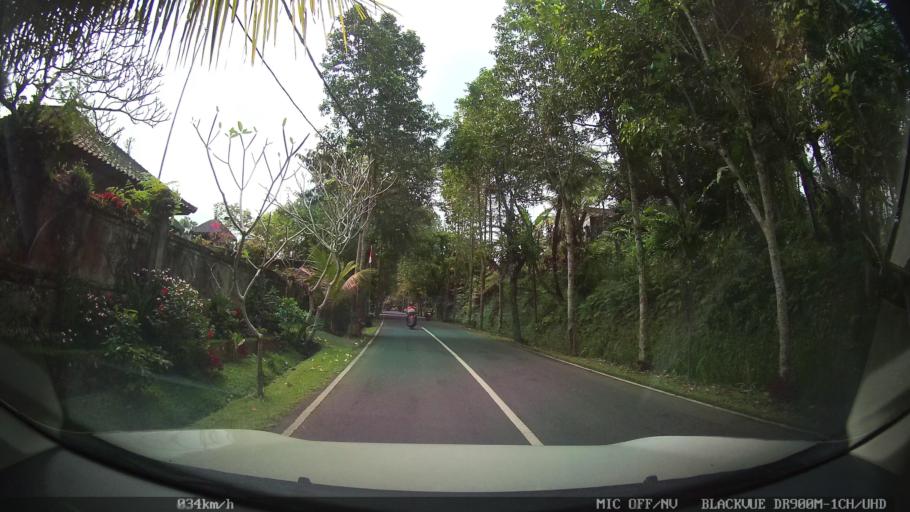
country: ID
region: Bali
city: Petang
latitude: -8.3864
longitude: 115.2203
